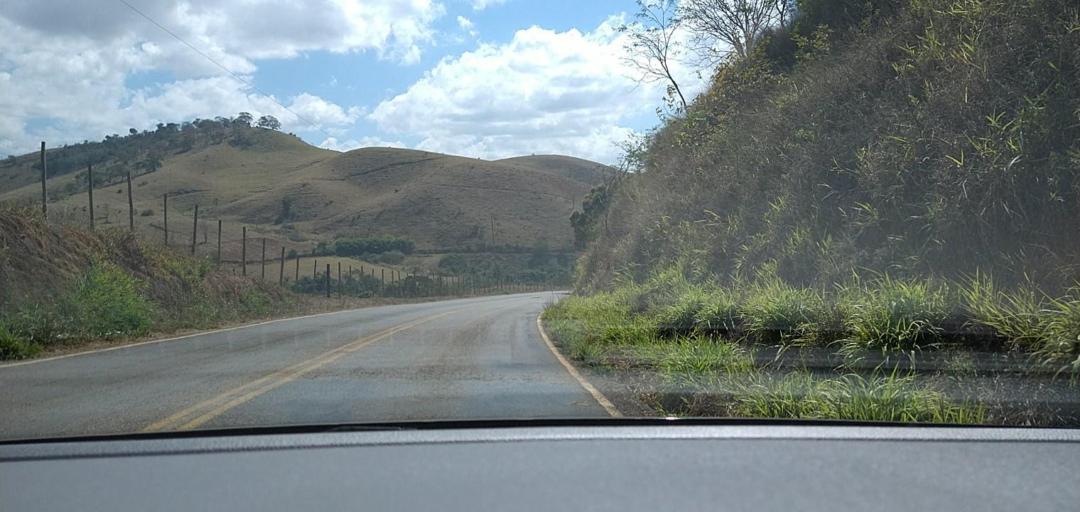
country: BR
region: Minas Gerais
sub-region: Ponte Nova
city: Ponte Nova
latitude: -20.2609
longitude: -42.8883
